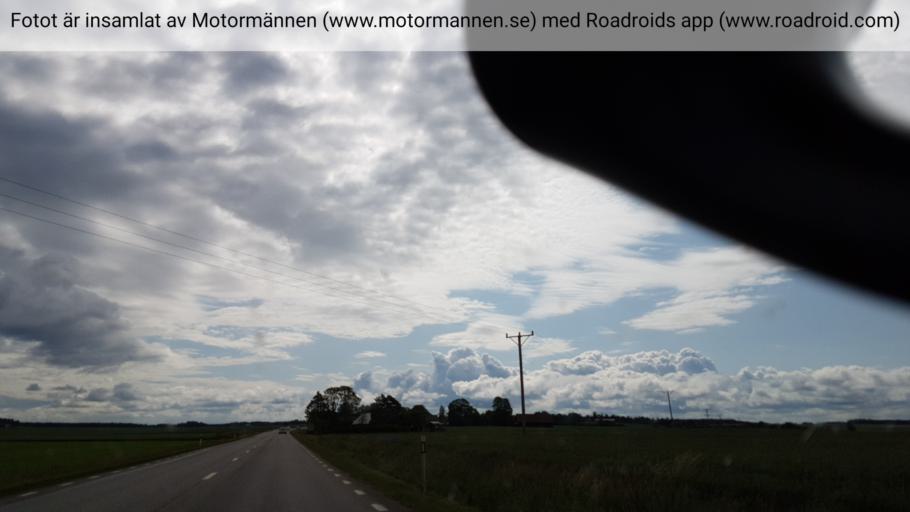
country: SE
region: Vaestra Goetaland
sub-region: Vara Kommun
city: Kvanum
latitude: 58.2304
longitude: 13.1435
